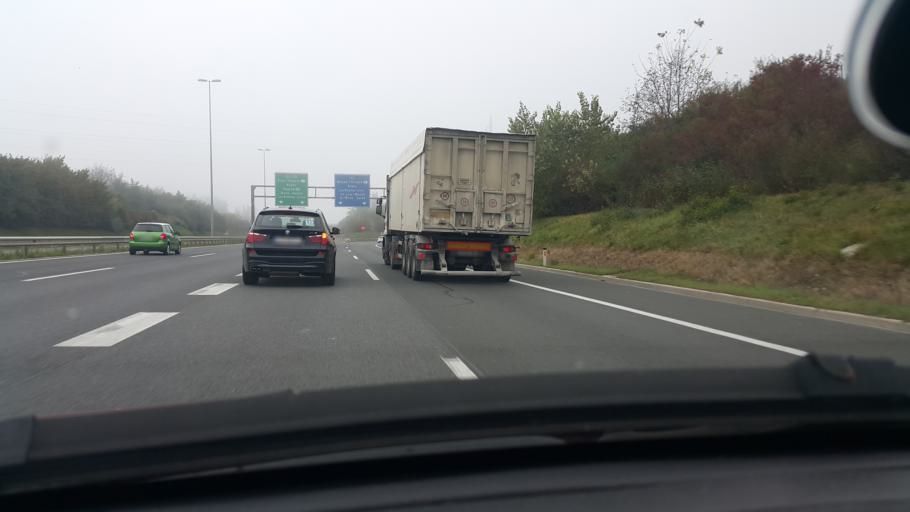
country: SI
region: Dol pri Ljubljani
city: Dol pri Ljubljani
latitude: 46.0700
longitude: 14.5774
